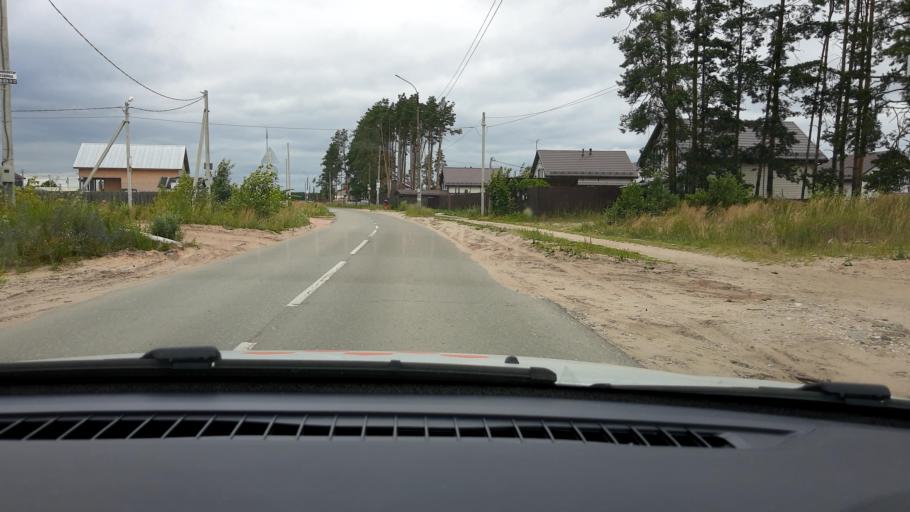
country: RU
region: Nizjnij Novgorod
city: Pyra
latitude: 56.2407
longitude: 43.3874
